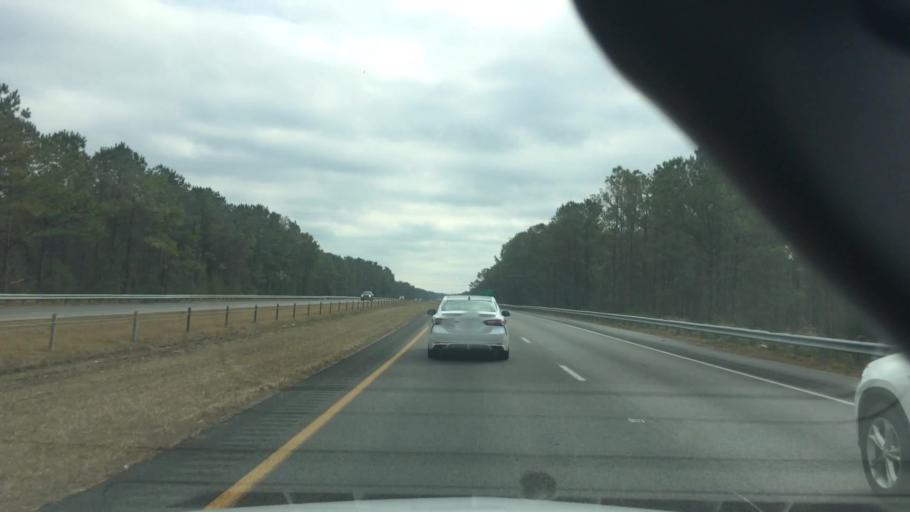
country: US
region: North Carolina
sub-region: New Hanover County
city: Castle Hayne
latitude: 34.3573
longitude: -77.8873
